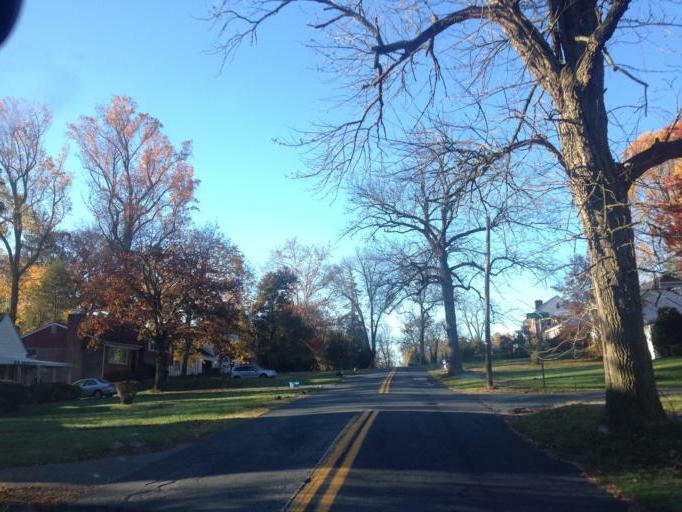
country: US
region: Maryland
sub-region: Baltimore County
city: Lochearn
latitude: 39.3504
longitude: -76.7385
